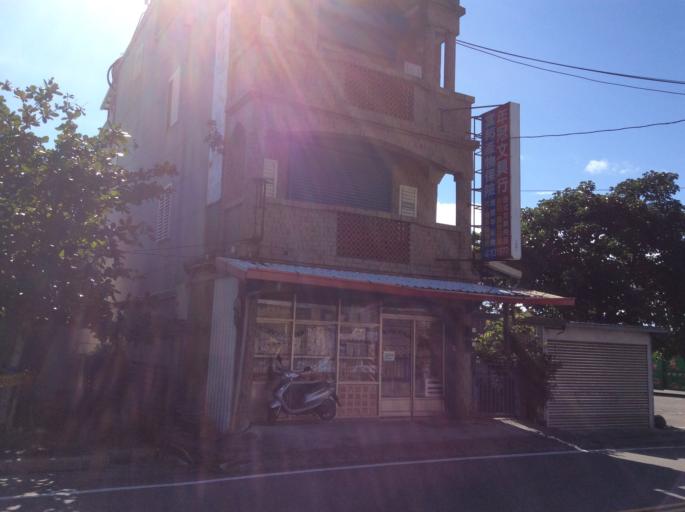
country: TW
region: Taiwan
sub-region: Taitung
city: Taitung
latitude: 23.3152
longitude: 121.4520
